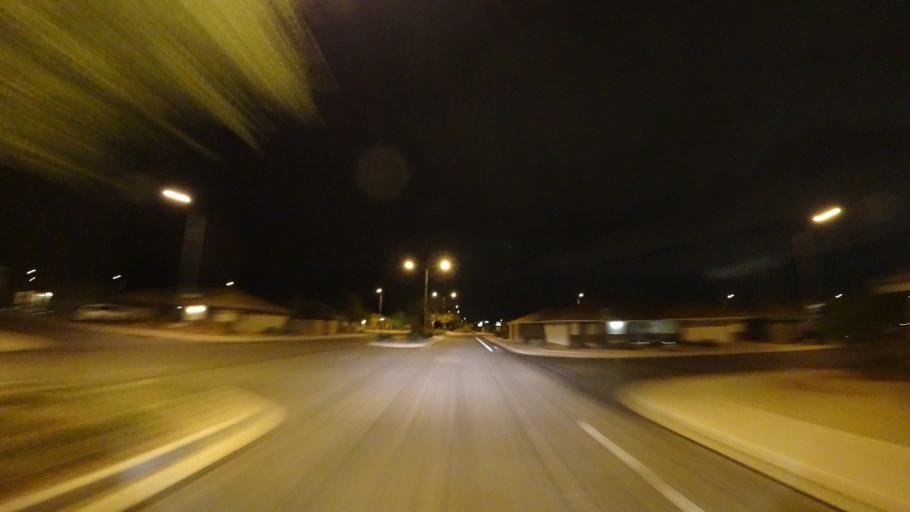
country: US
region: Arizona
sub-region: Pinal County
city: Apache Junction
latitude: 33.3667
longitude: -111.5883
